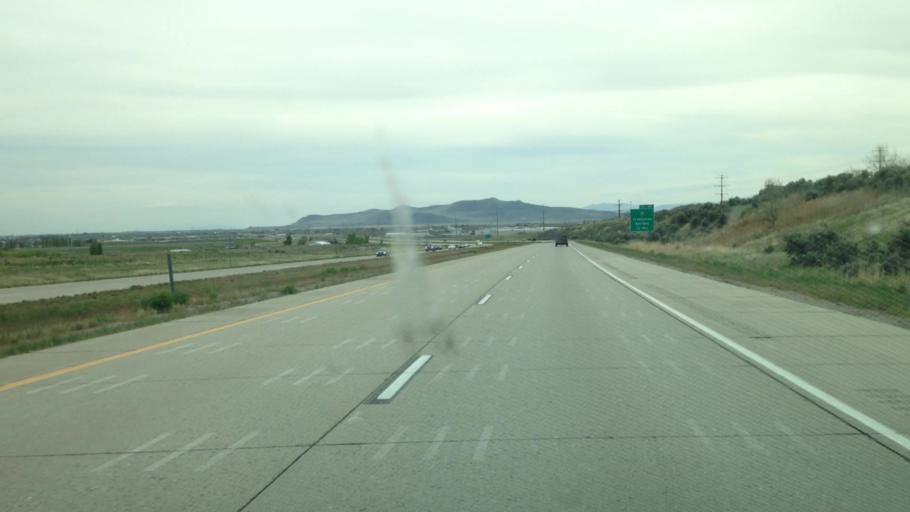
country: US
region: Utah
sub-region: Box Elder County
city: Garland
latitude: 41.7390
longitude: -112.1899
